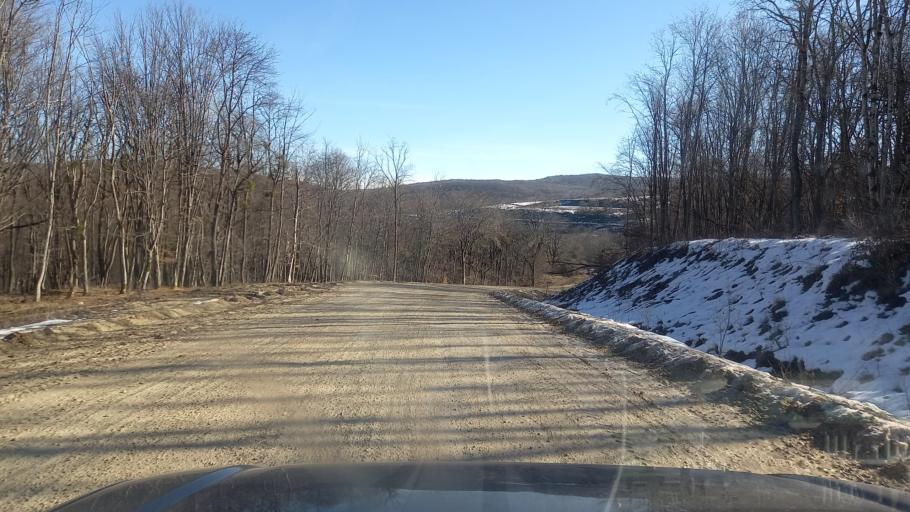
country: RU
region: Adygeya
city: Kamennomostskiy
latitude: 44.2813
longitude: 40.3233
